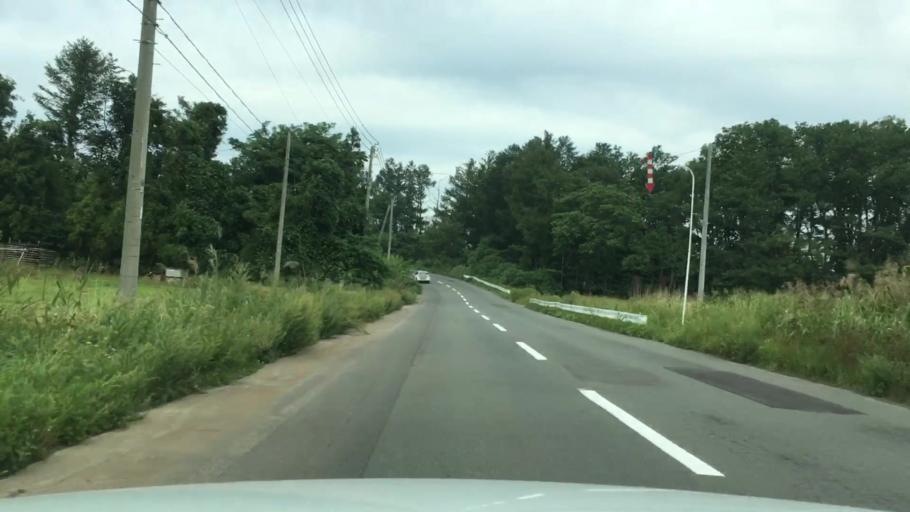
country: JP
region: Aomori
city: Shimokizukuri
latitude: 40.6846
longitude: 140.3695
